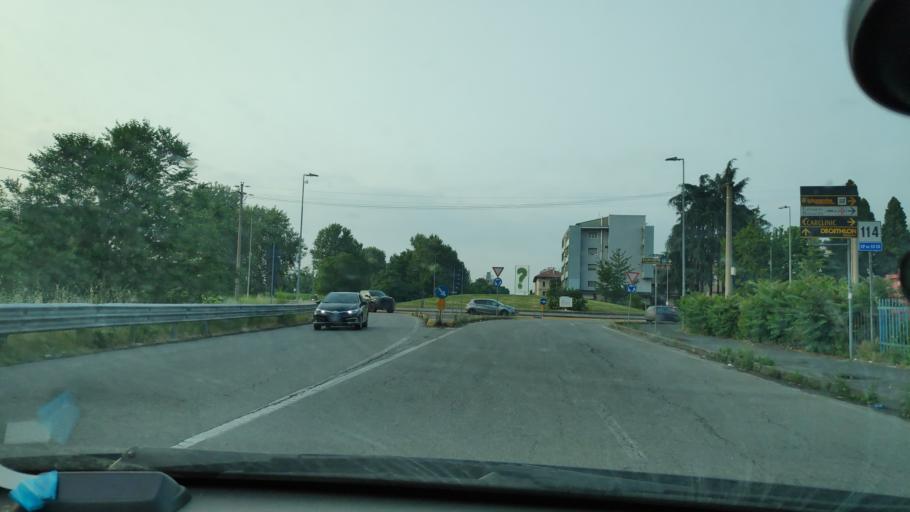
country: IT
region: Lombardy
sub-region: Citta metropolitana di Milano
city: Rozzano
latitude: 45.3861
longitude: 9.1466
